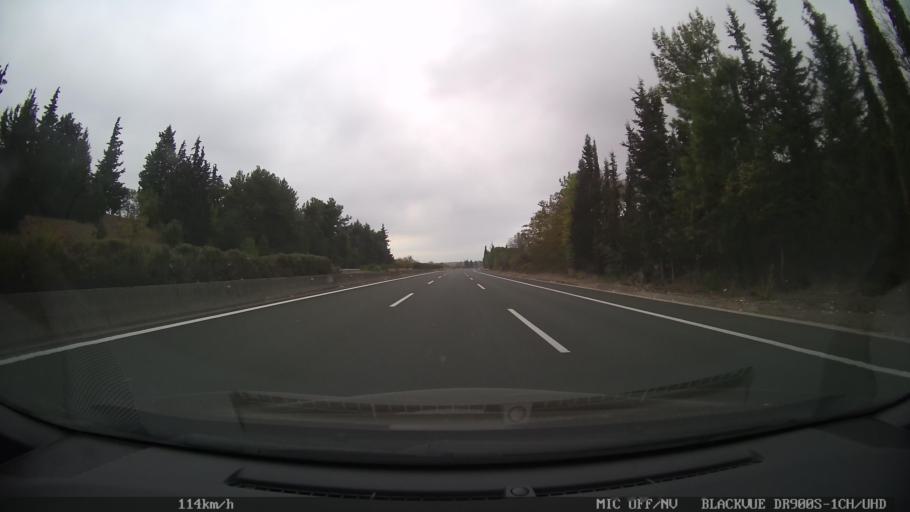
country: GR
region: Central Macedonia
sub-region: Nomos Pierias
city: Kitros
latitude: 40.3639
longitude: 22.6035
